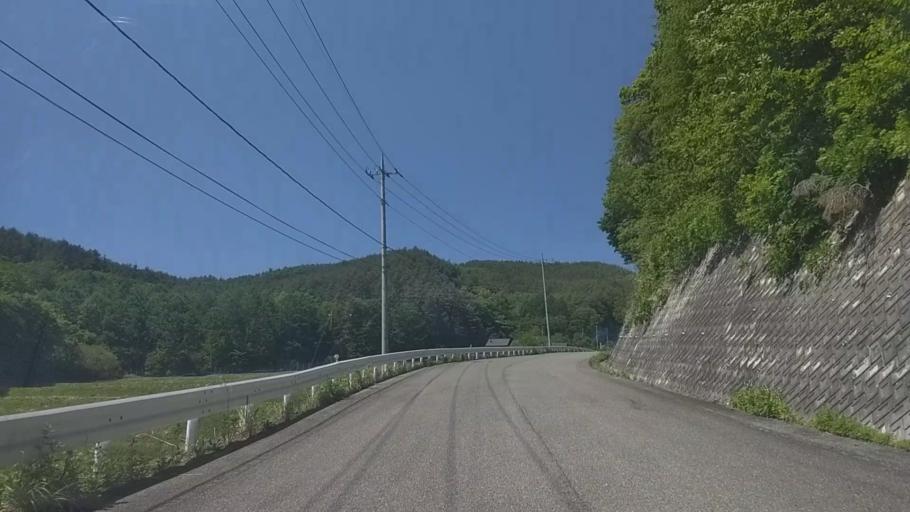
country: JP
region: Yamanashi
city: Nirasaki
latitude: 35.8587
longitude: 138.4472
